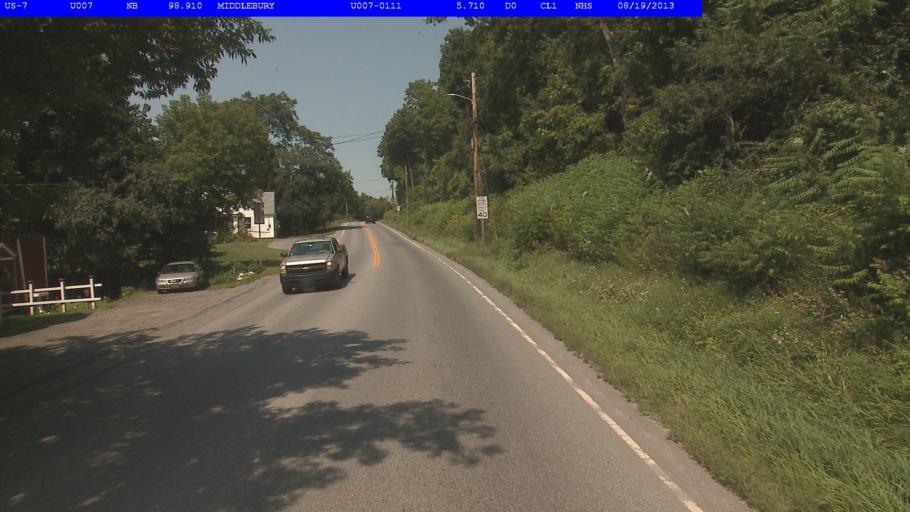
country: US
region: Vermont
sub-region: Addison County
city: Middlebury (village)
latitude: 44.0230
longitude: -73.1657
